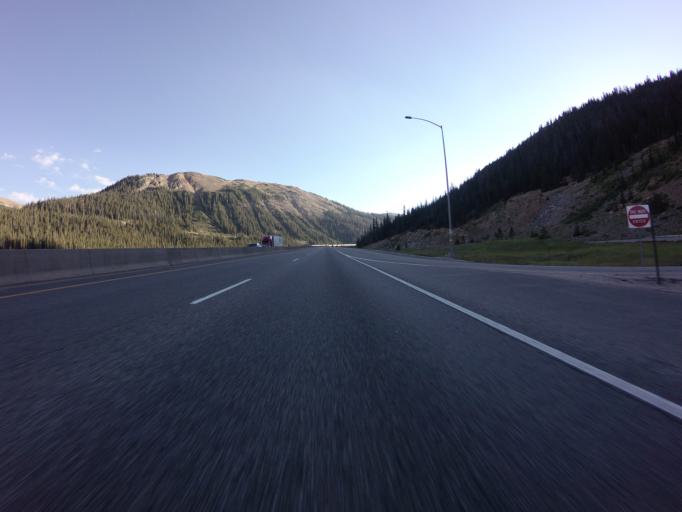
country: US
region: Colorado
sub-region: Summit County
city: Keystone
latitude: 39.6856
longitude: -105.8853
